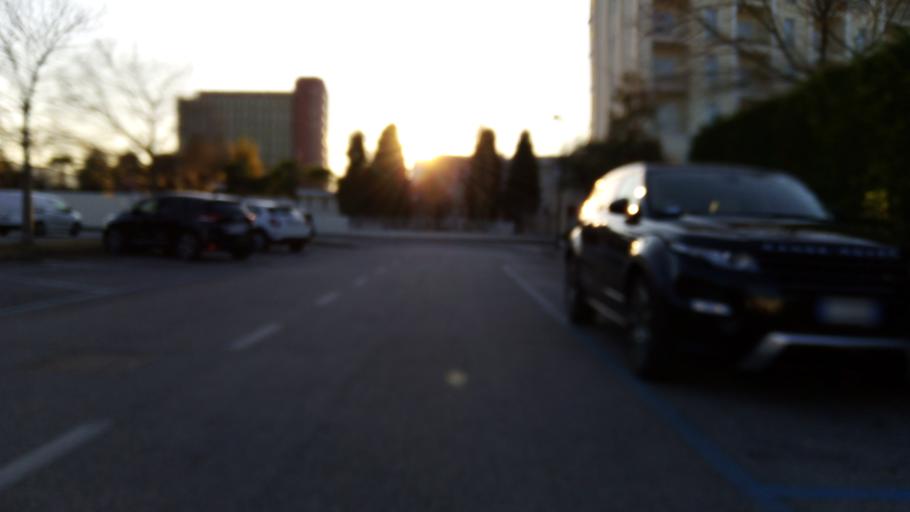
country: IT
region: Veneto
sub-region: Provincia di Padova
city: Abano Terme
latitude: 45.3526
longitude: 11.7835
